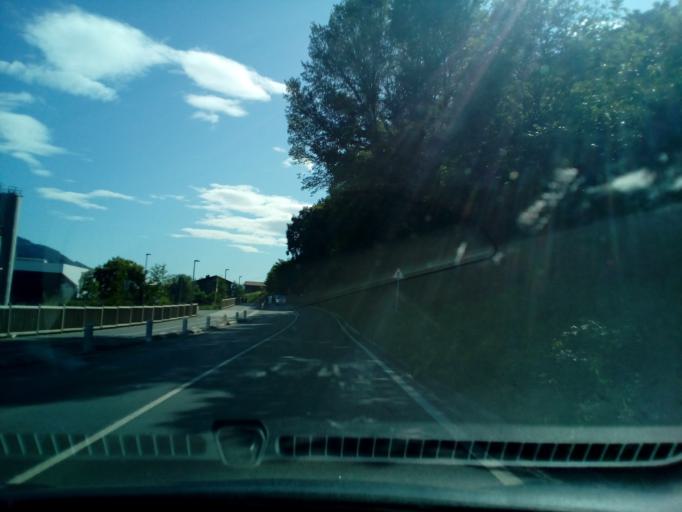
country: ES
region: Basque Country
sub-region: Provincia de Guipuzcoa
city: Aduna
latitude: 43.2080
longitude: -2.0390
